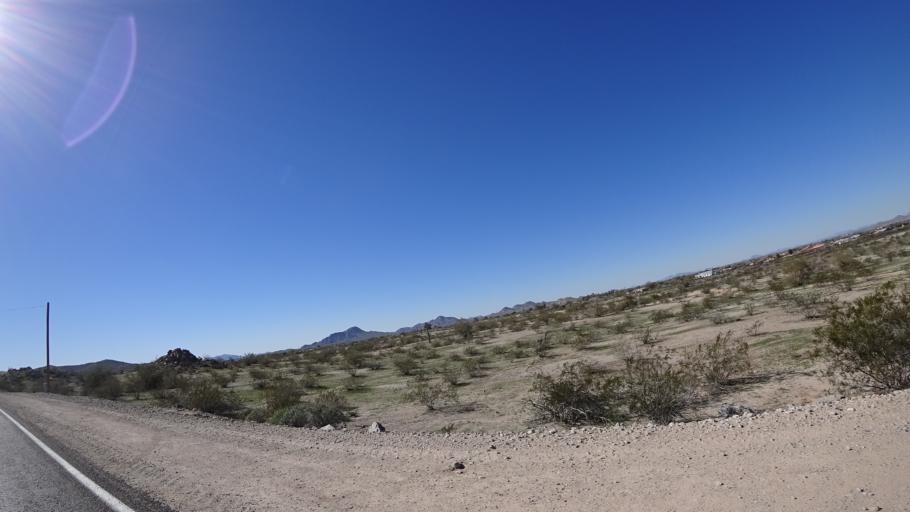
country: US
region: Arizona
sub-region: Maricopa County
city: Buckeye
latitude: 33.3303
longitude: -112.4701
